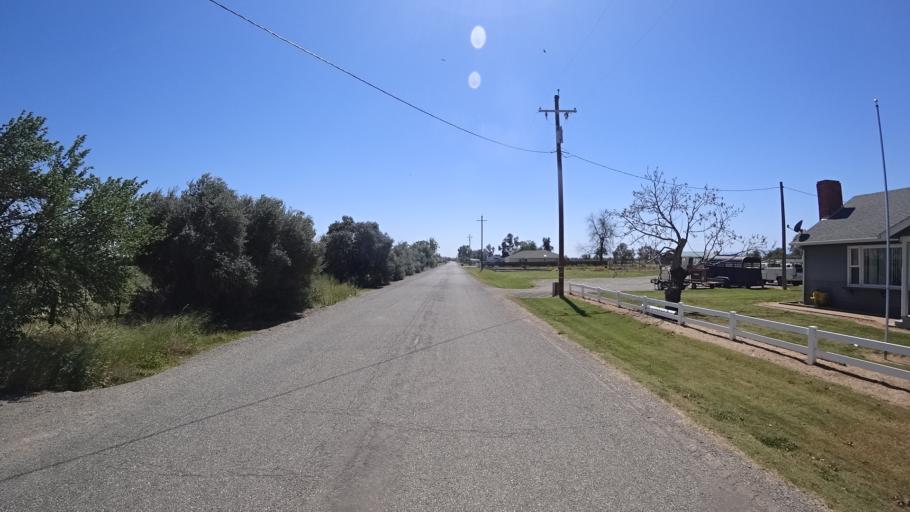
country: US
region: California
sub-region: Glenn County
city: Orland
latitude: 39.7922
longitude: -122.1784
